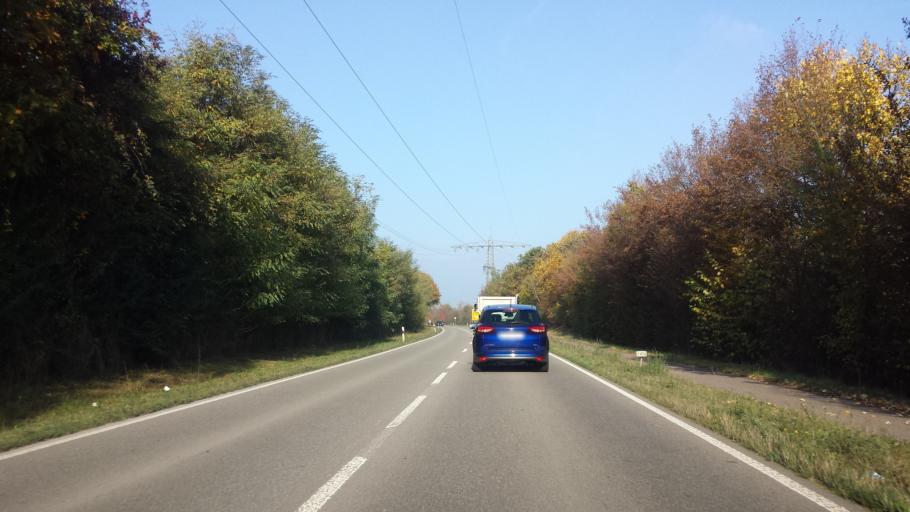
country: DE
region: Baden-Wuerttemberg
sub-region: Karlsruhe Region
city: Kronau
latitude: 49.2084
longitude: 8.6268
